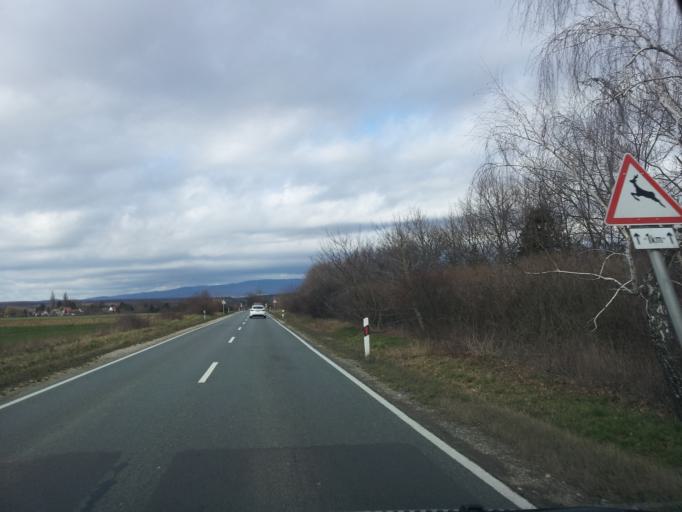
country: HU
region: Vas
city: Gencsapati
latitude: 47.3053
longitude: 16.6010
